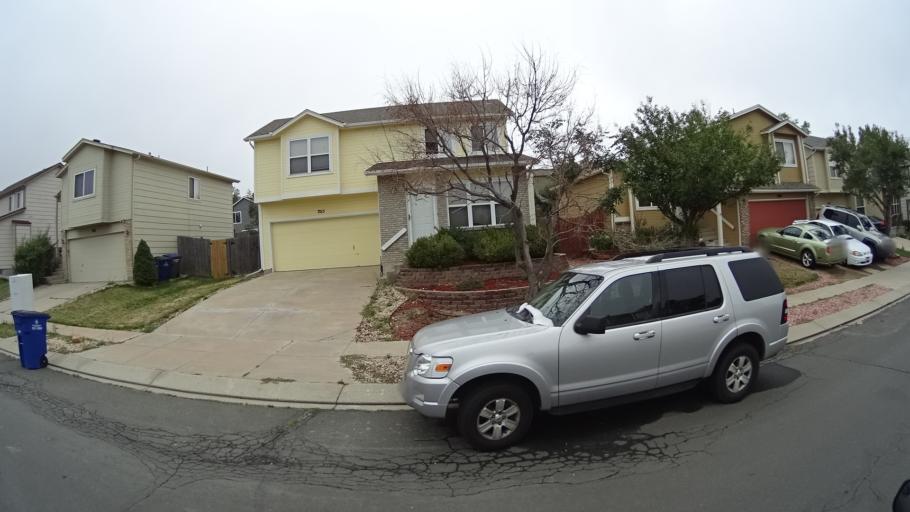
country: US
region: Colorado
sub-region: El Paso County
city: Black Forest
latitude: 38.9378
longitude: -104.7419
